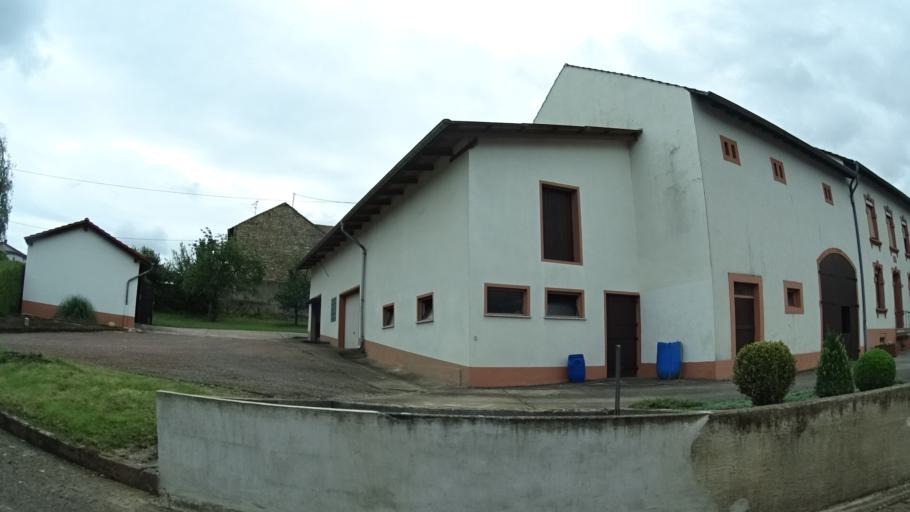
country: DE
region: Saarland
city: Mettlach
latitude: 49.4459
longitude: 6.5547
